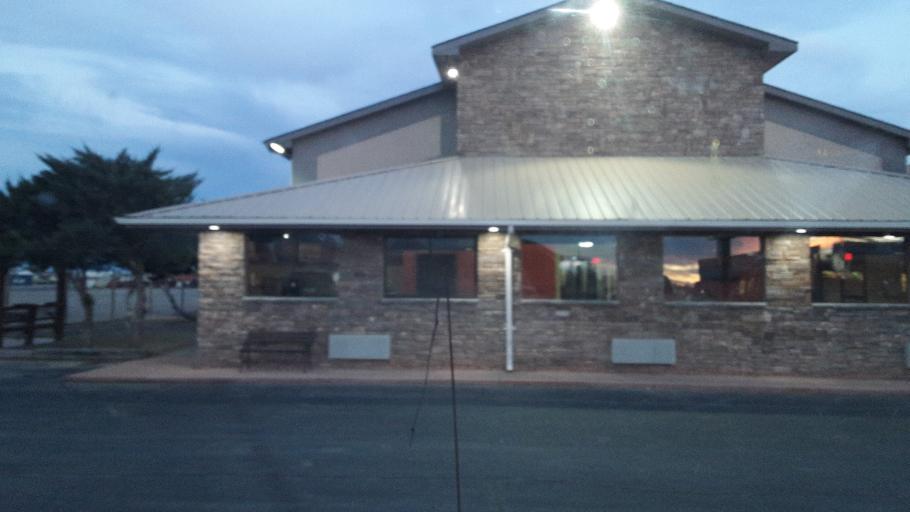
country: US
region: Colorado
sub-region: Prowers County
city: Lamar
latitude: 38.1008
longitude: -102.6181
